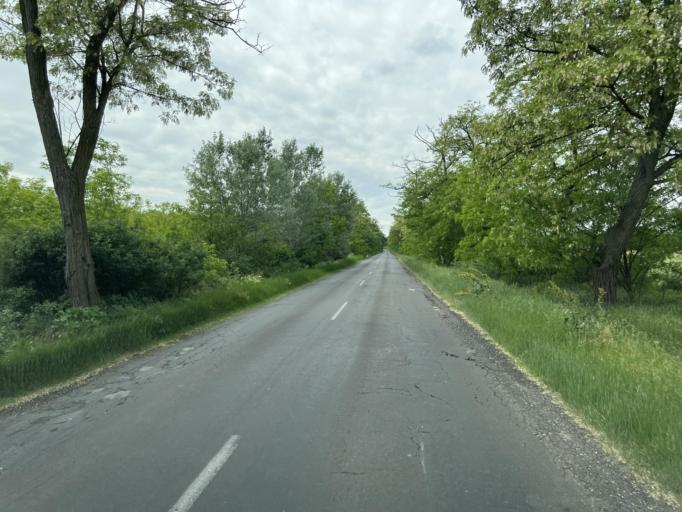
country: HU
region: Pest
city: Tapioszecso
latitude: 47.4668
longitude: 19.6148
